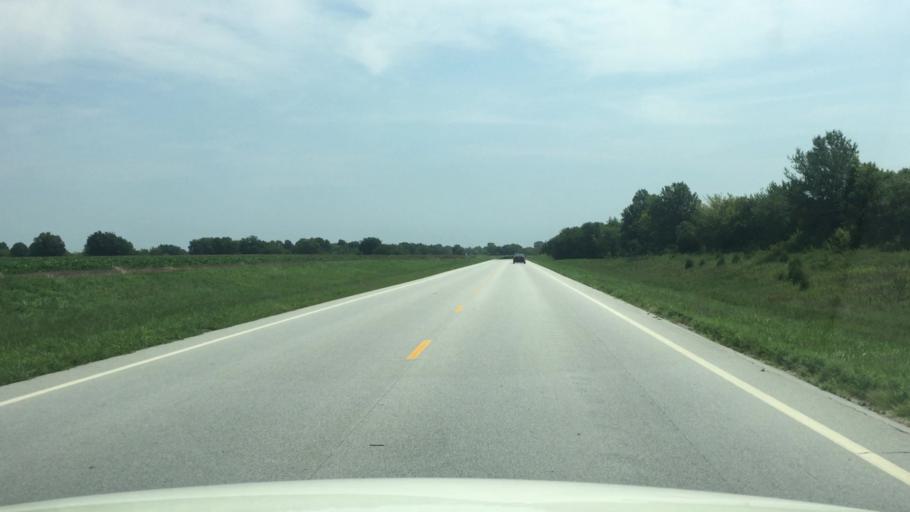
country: US
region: Kansas
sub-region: Cherokee County
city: Columbus
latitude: 37.1797
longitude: -94.9667
